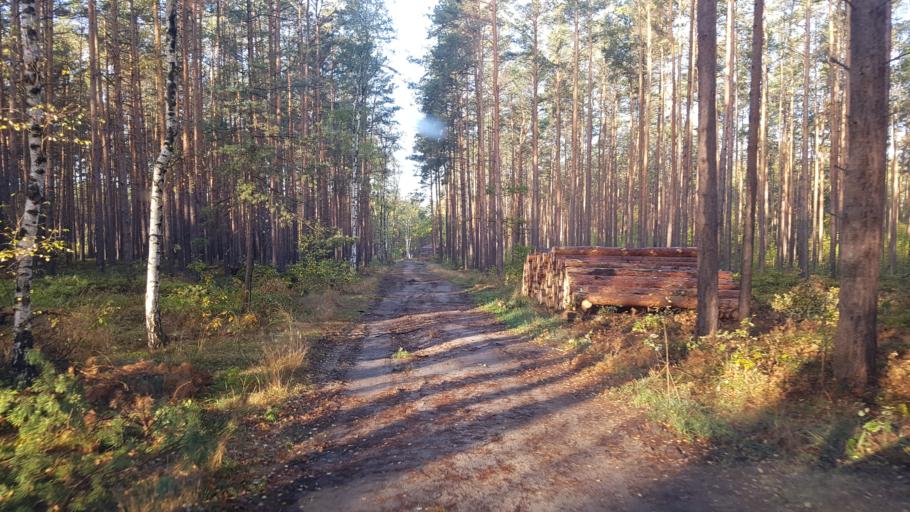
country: DE
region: Brandenburg
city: Ruckersdorf
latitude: 51.5924
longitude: 13.5959
